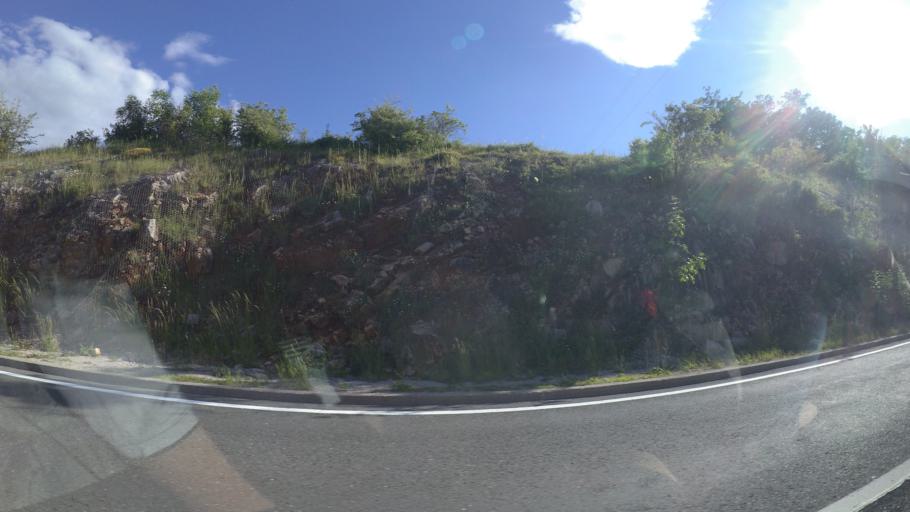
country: BA
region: Federation of Bosnia and Herzegovina
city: Bihac
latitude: 44.6822
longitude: 15.7314
